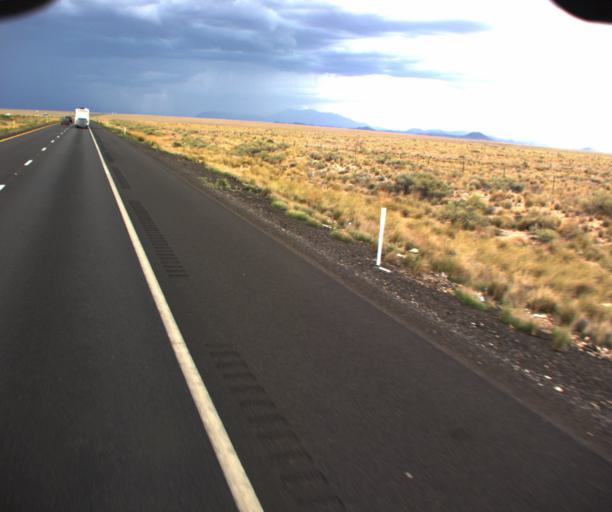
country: US
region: Arizona
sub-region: Coconino County
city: LeChee
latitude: 35.1181
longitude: -111.1271
